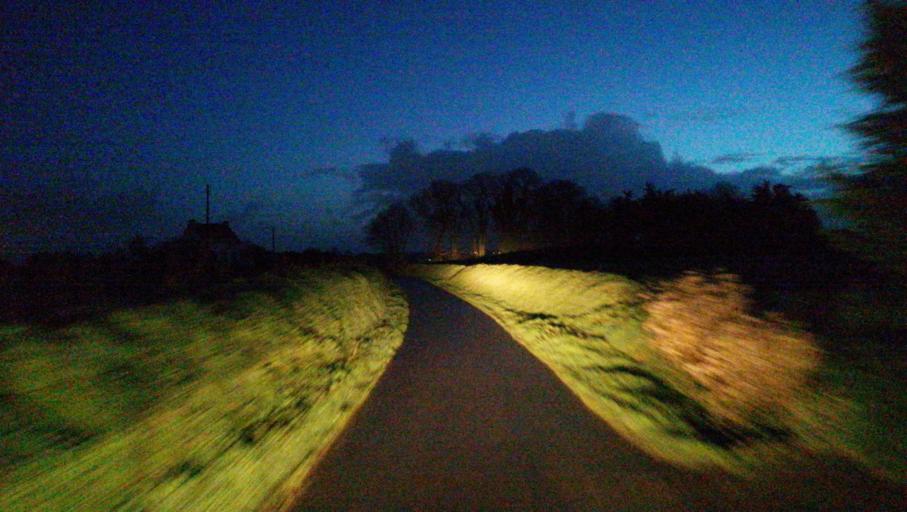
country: FR
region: Brittany
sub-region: Departement des Cotes-d'Armor
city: Pommerit-le-Vicomte
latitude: 48.6576
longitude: -3.0570
